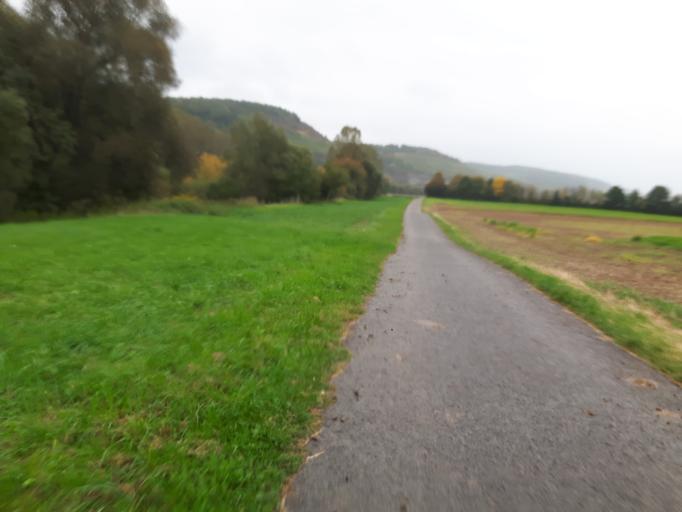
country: DE
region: Bavaria
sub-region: Regierungsbezirk Unterfranken
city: Karlstadt
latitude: 49.9437
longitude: 9.7882
